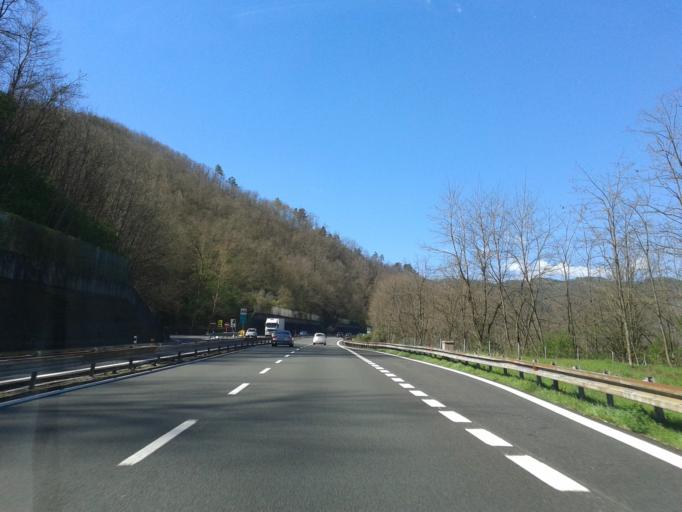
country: IT
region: Liguria
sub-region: Provincia di La Spezia
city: Carrodano
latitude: 44.2307
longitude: 9.6302
